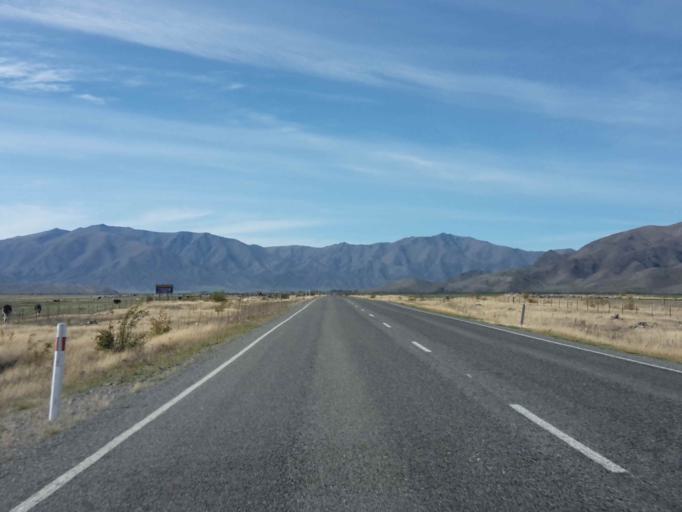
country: NZ
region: Otago
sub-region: Queenstown-Lakes District
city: Wanaka
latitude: -44.5047
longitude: 169.8784
